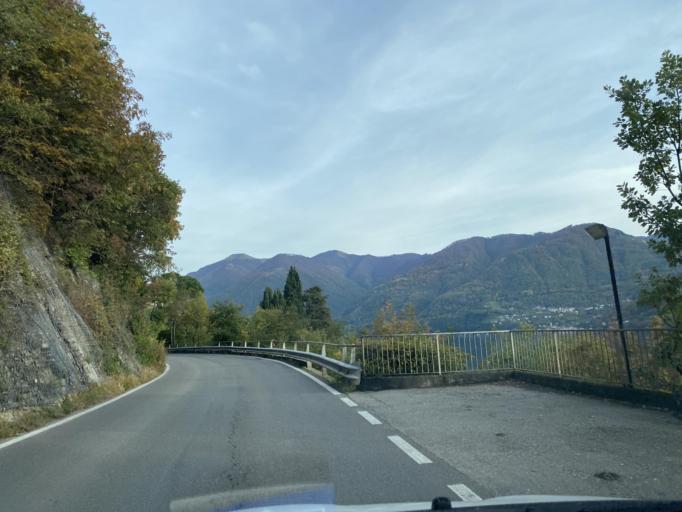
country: IT
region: Lombardy
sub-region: Provincia di Como
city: San Mamete
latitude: 46.0242
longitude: 9.0571
